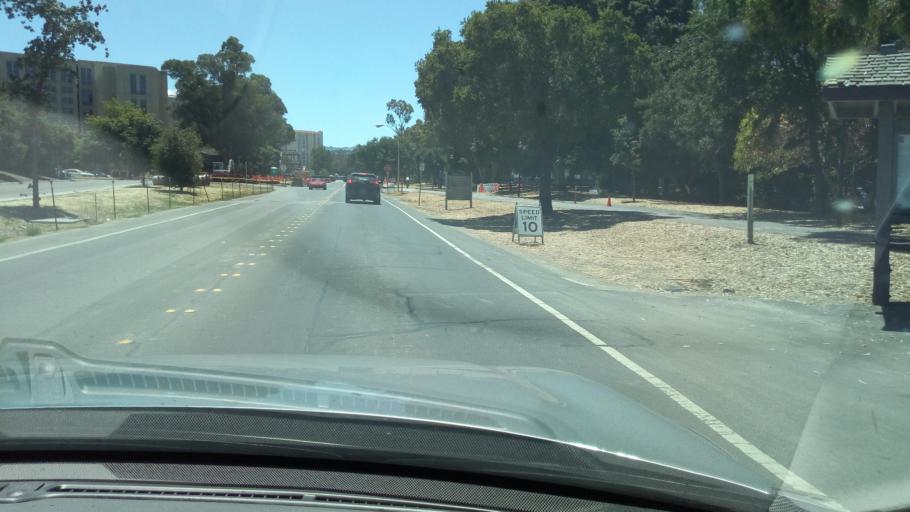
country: US
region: California
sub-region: Santa Clara County
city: Stanford
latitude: 37.4296
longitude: -122.1545
